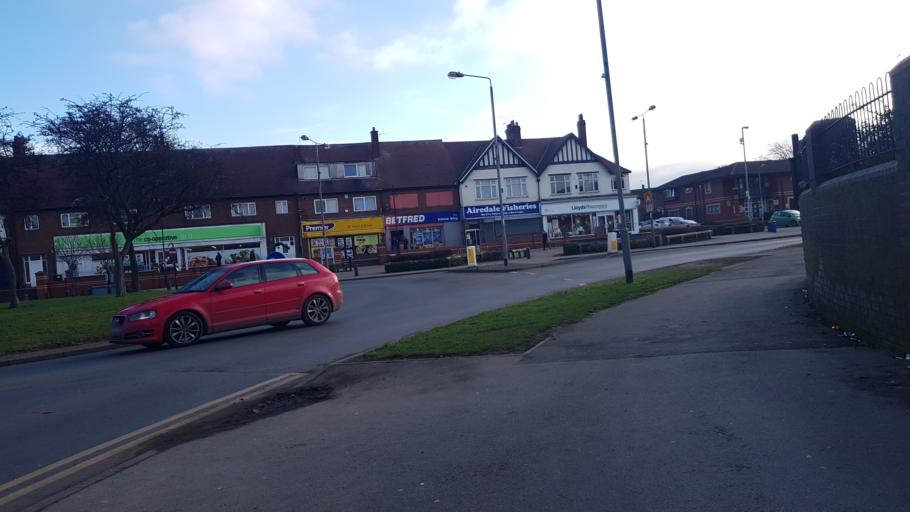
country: GB
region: England
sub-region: City and Borough of Wakefield
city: Pontefract
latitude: 53.7240
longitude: -1.3157
